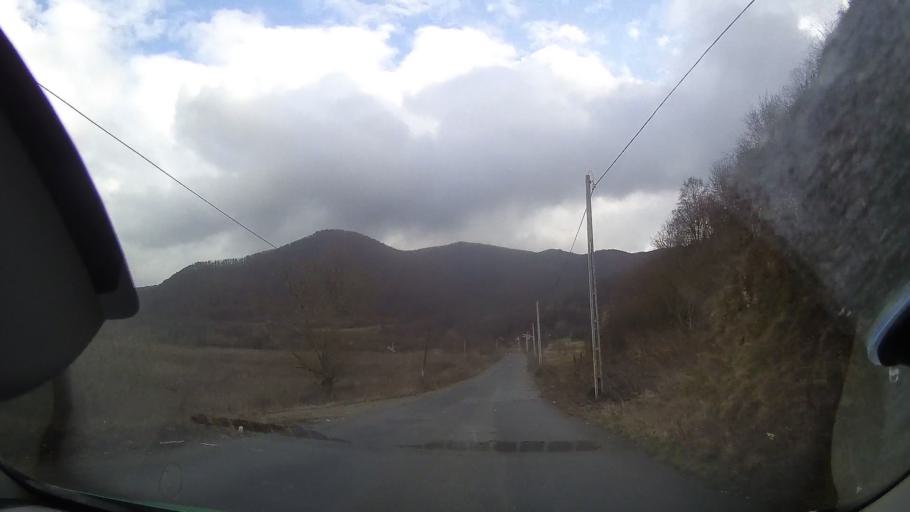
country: RO
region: Cluj
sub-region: Comuna Moldovenesti
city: Moldovenesti
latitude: 46.5046
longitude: 23.6025
